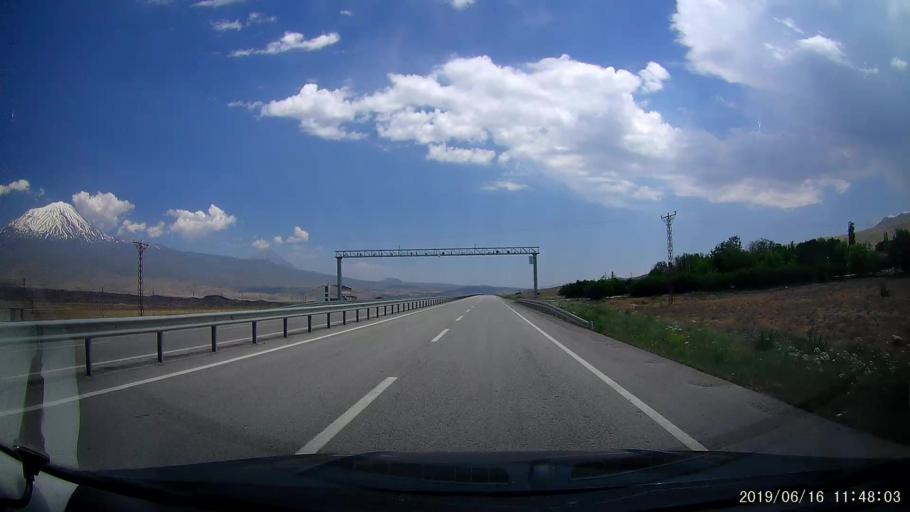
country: TR
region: Agri
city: Dogubayazit
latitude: 39.5582
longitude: 44.1376
